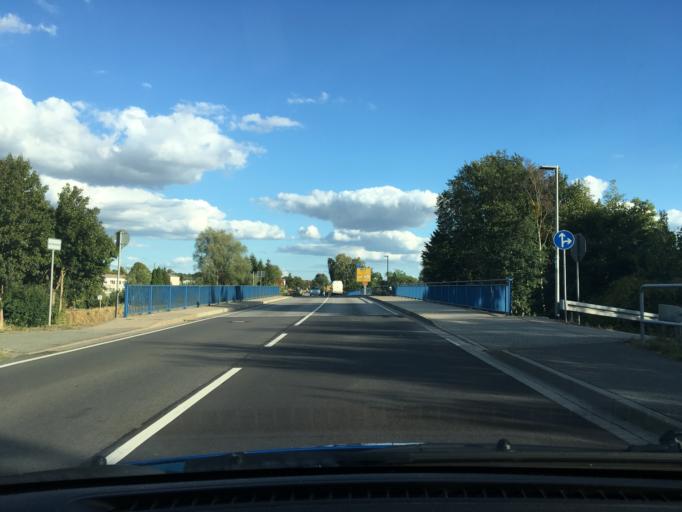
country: DE
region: Mecklenburg-Vorpommern
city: Grabow
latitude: 53.2768
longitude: 11.5568
